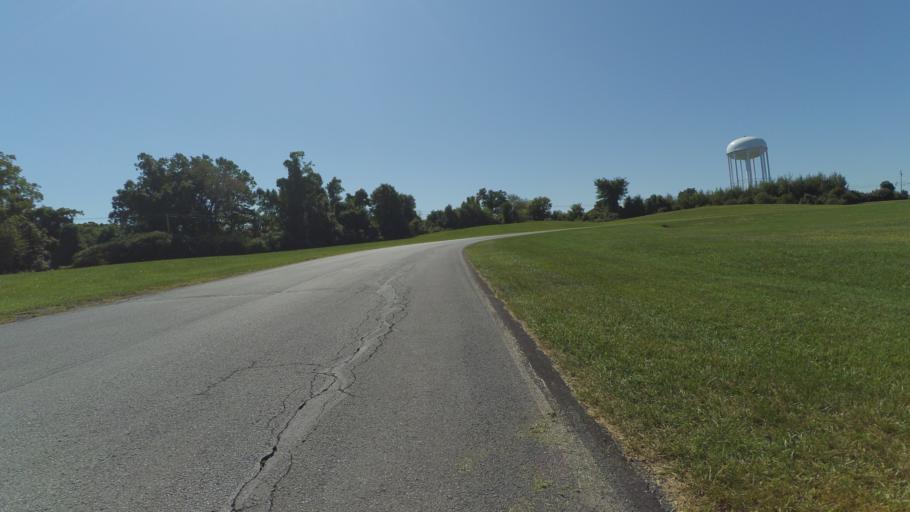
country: US
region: Pennsylvania
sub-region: Centre County
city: State College
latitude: 40.7744
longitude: -77.8940
